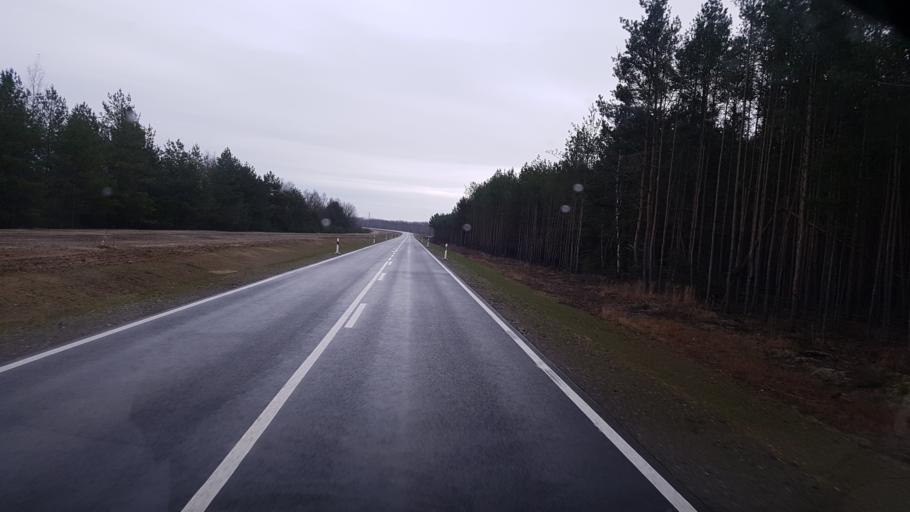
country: DE
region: Brandenburg
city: Lauchhammer
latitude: 51.5203
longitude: 13.7931
